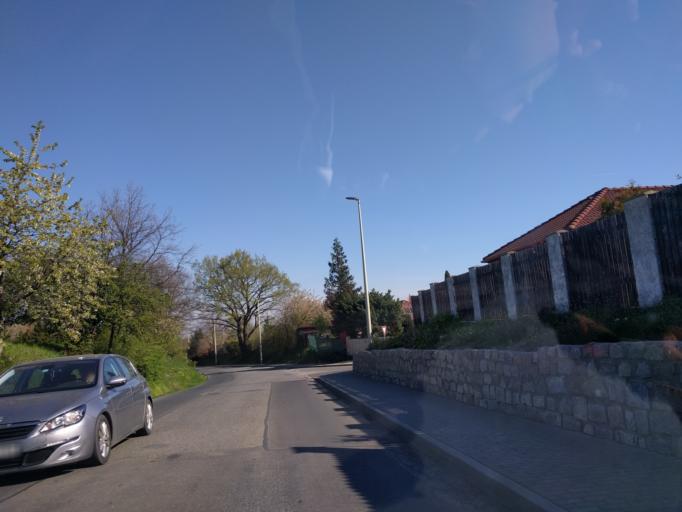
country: CZ
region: Central Bohemia
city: Mukarov
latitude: 50.0199
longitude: 14.7879
